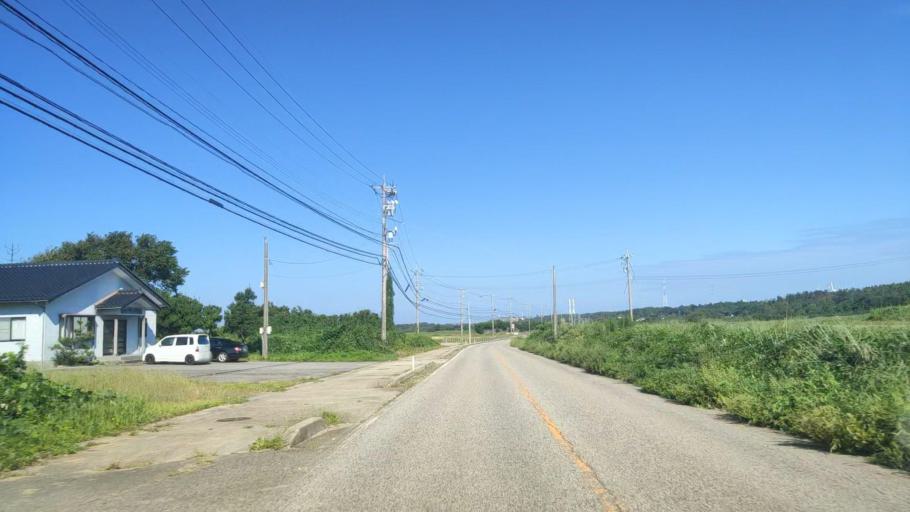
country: JP
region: Ishikawa
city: Hakui
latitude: 37.0391
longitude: 136.7427
